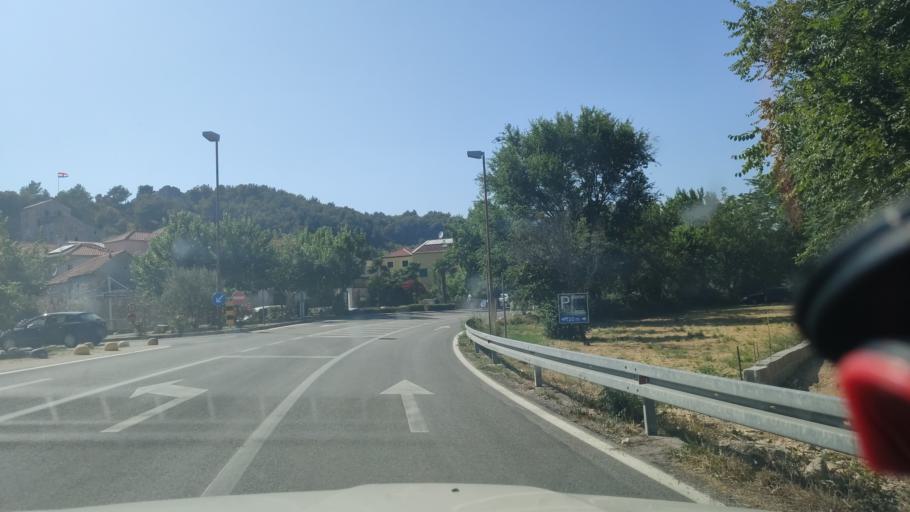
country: HR
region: Sibensko-Kniniska
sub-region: Grad Sibenik
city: Sibenik
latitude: 43.8180
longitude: 15.9247
